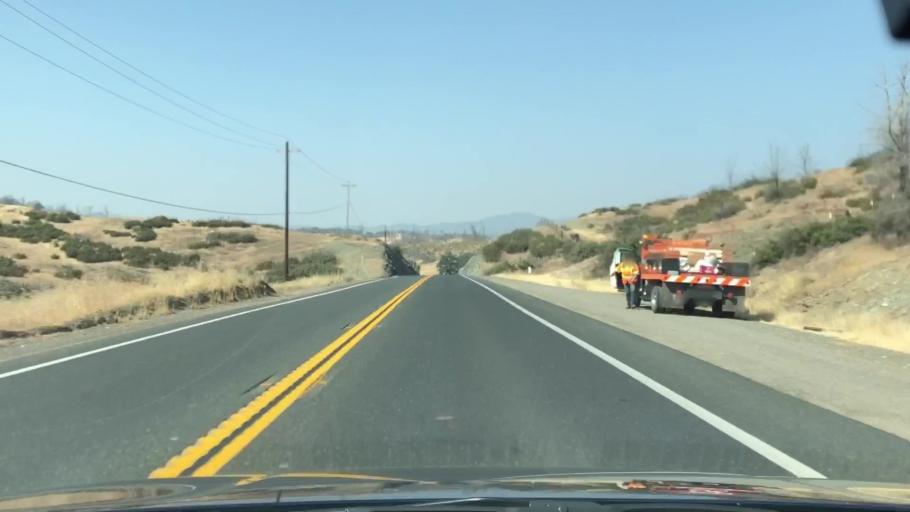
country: US
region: California
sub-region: Lake County
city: Hidden Valley Lake
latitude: 38.7767
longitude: -122.5780
